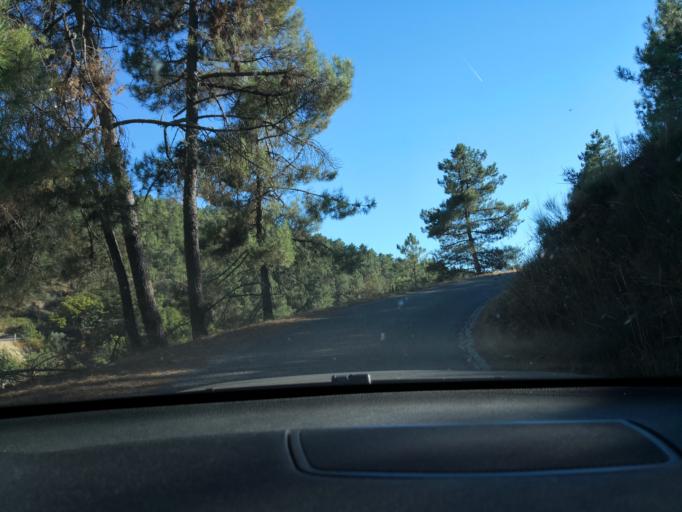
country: PT
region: Vila Real
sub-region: Sabrosa
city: Vilela
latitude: 41.2247
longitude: -7.5828
